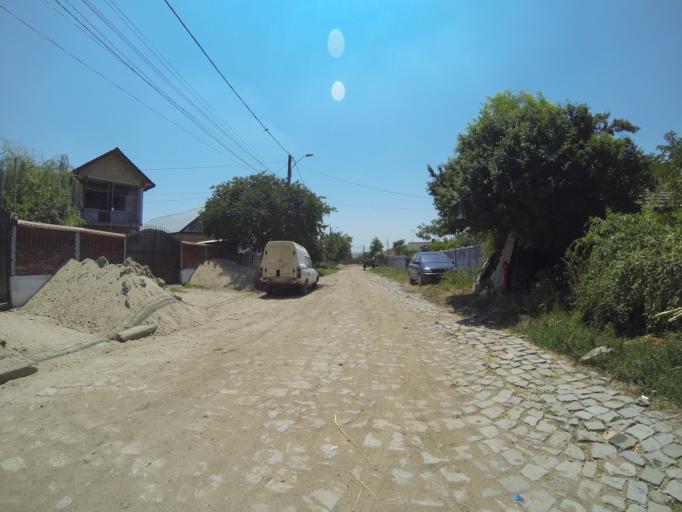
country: RO
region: Dolj
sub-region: Comuna Segarcea
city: Segarcea
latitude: 44.0892
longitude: 23.7536
